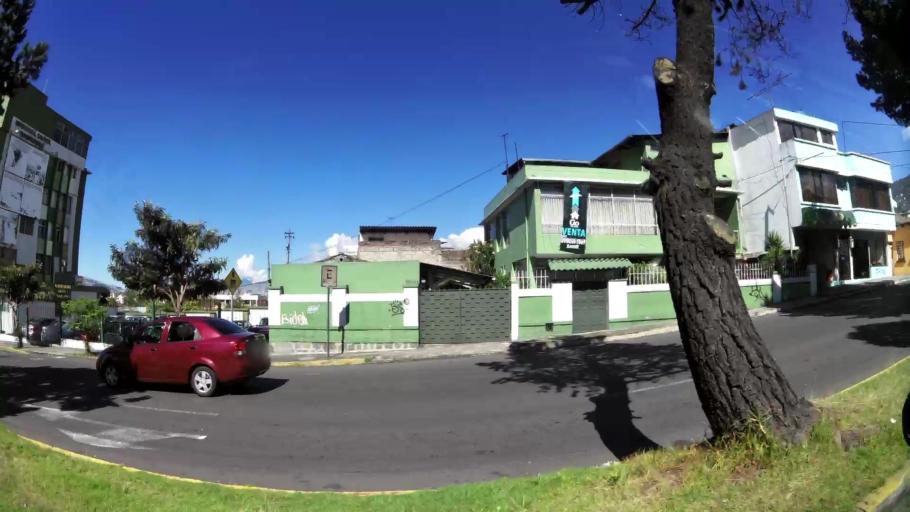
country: EC
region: Pichincha
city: Quito
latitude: -0.2374
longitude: -78.5258
